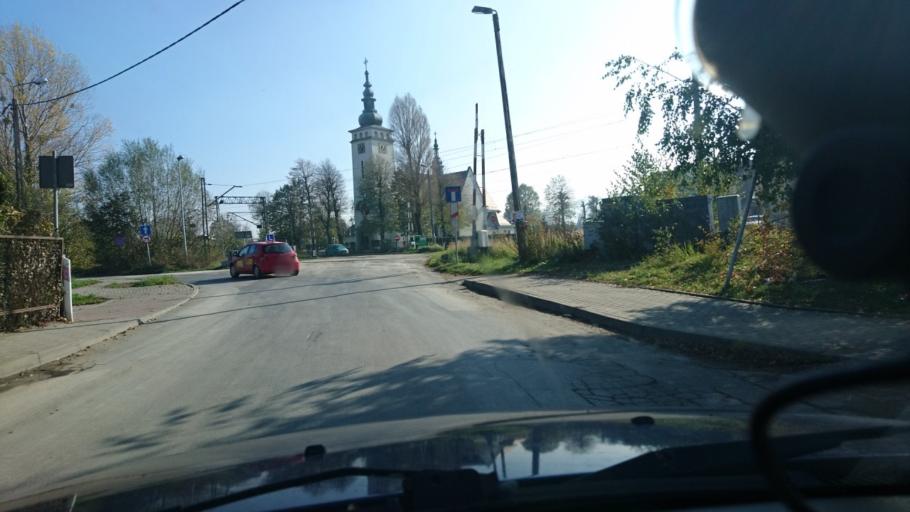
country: PL
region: Silesian Voivodeship
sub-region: Powiat bielski
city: Jaworze
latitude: 49.8114
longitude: 18.9776
